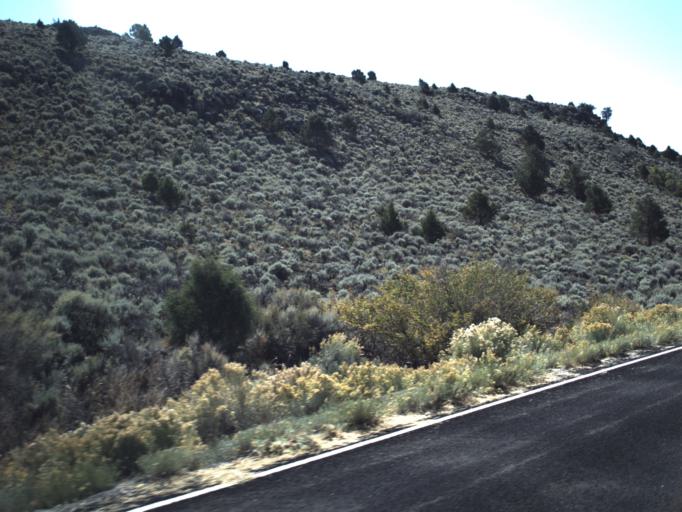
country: US
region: Utah
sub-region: Wayne County
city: Loa
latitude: 38.4761
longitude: -111.8303
